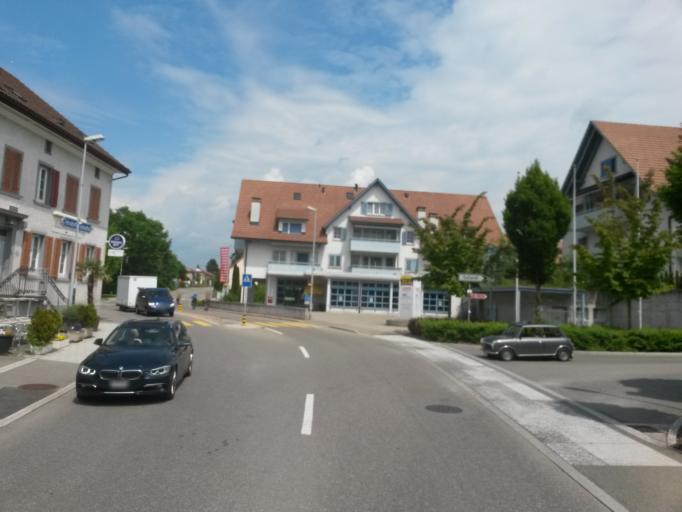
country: CH
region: Zurich
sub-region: Bezirk Pfaeffikon
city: Russikon
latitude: 47.3940
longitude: 8.7763
